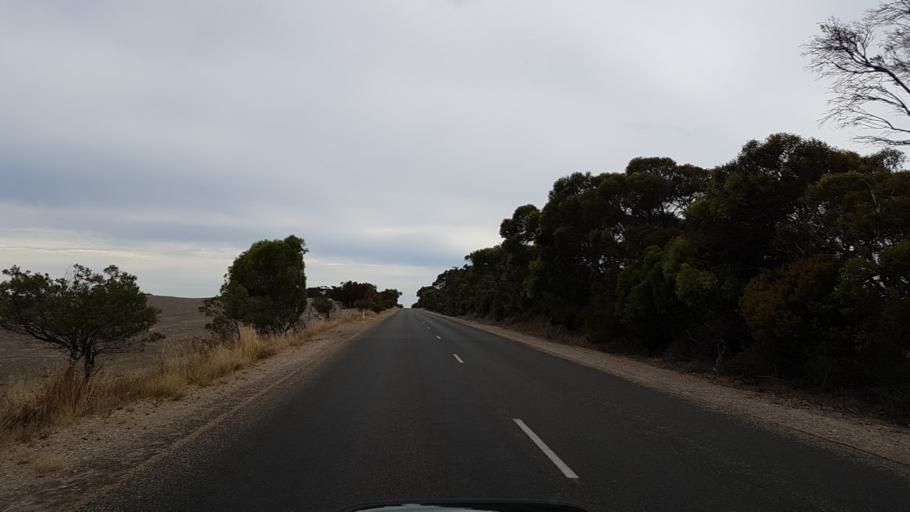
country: AU
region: South Australia
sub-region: Yorke Peninsula
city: Honiton
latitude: -34.9873
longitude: 137.1454
